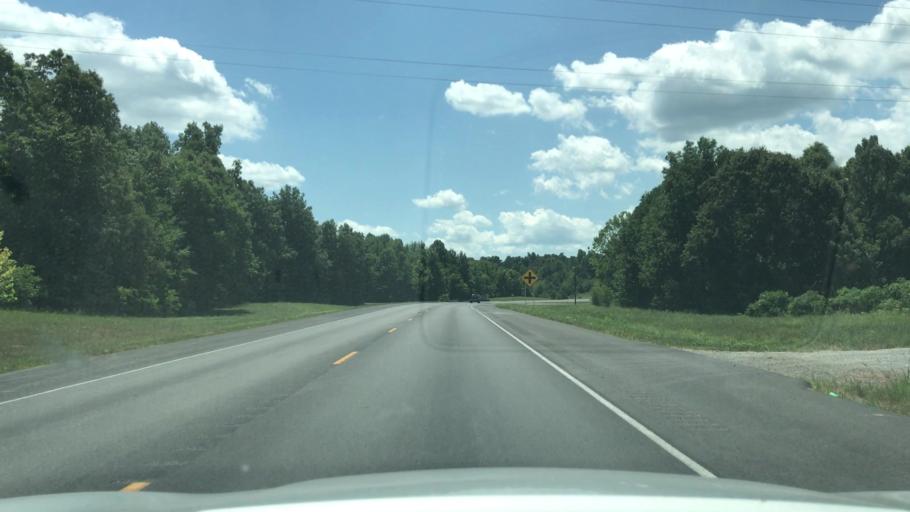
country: US
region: Kentucky
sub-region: Muhlenberg County
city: Greenville
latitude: 37.2069
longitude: -87.1952
